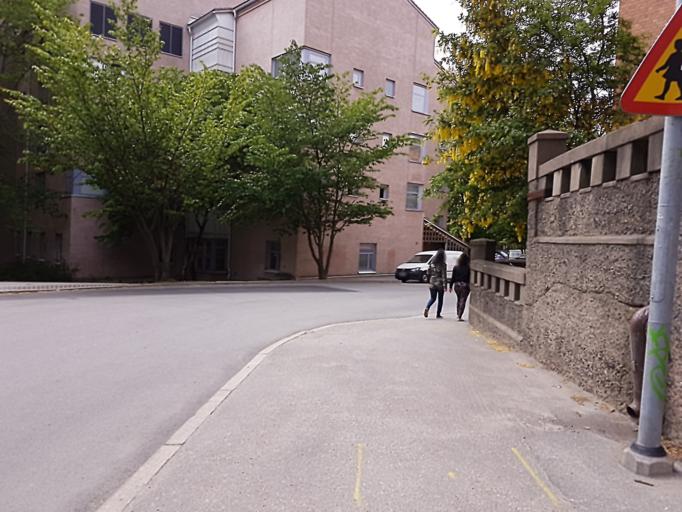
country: SE
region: Stockholm
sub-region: Solna Kommun
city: Rasunda
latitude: 59.3632
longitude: 17.9829
